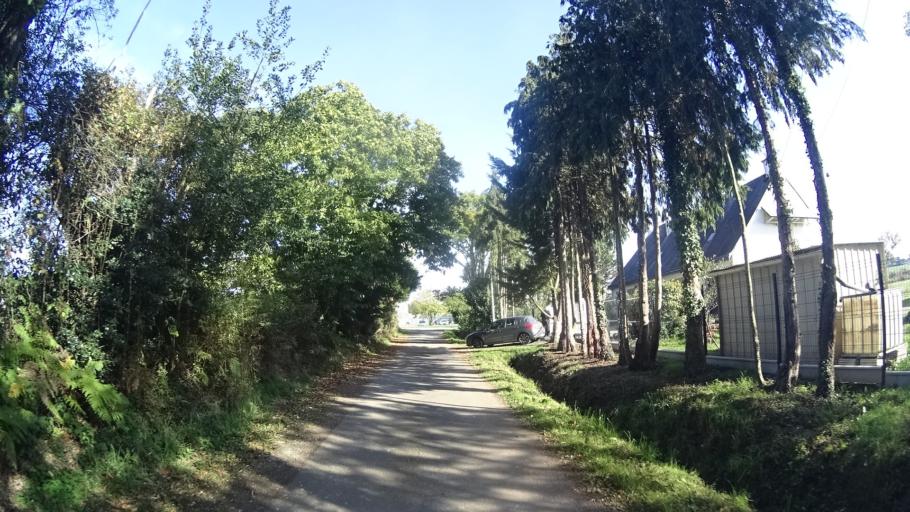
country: FR
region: Brittany
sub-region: Departement du Morbihan
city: Peillac
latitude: 47.7361
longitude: -2.2203
